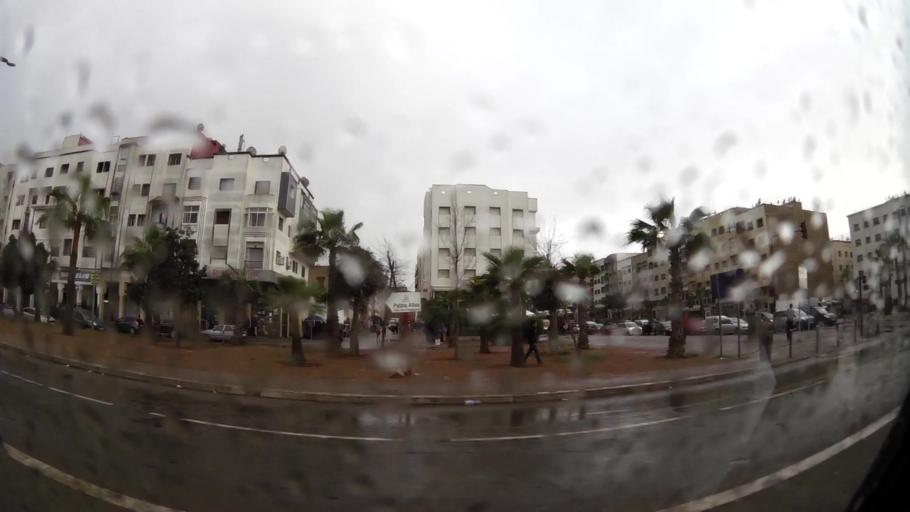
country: MA
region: Grand Casablanca
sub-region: Mediouna
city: Tit Mellil
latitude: 33.5724
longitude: -7.5305
